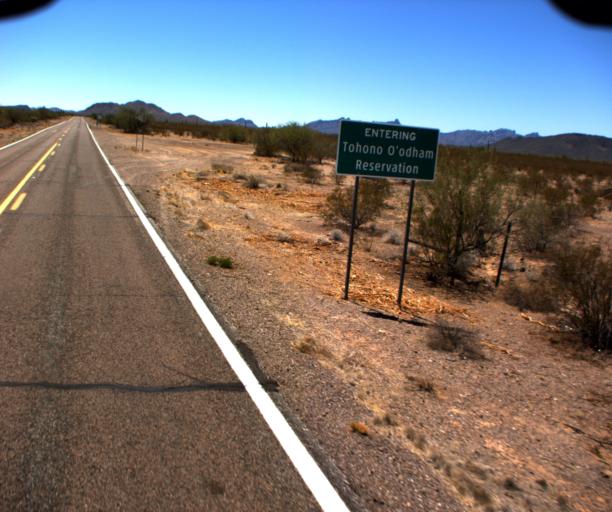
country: US
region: Arizona
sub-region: Pima County
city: Ajo
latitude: 32.2422
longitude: -112.7257
